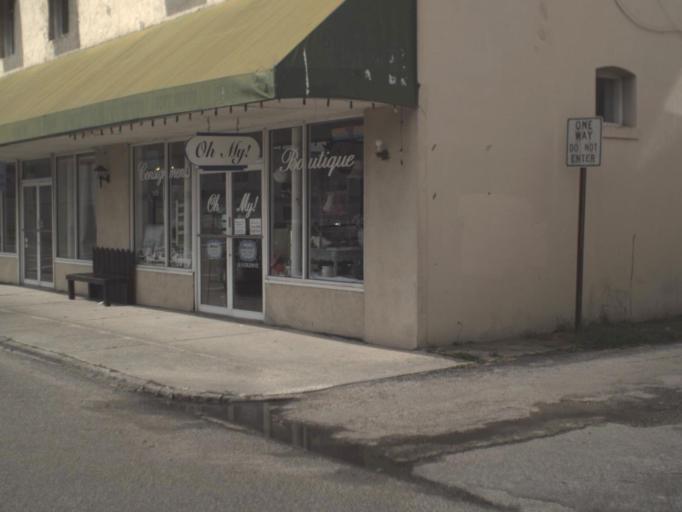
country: US
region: Florida
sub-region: Hillsborough County
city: Plant City
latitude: 28.0148
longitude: -82.1231
